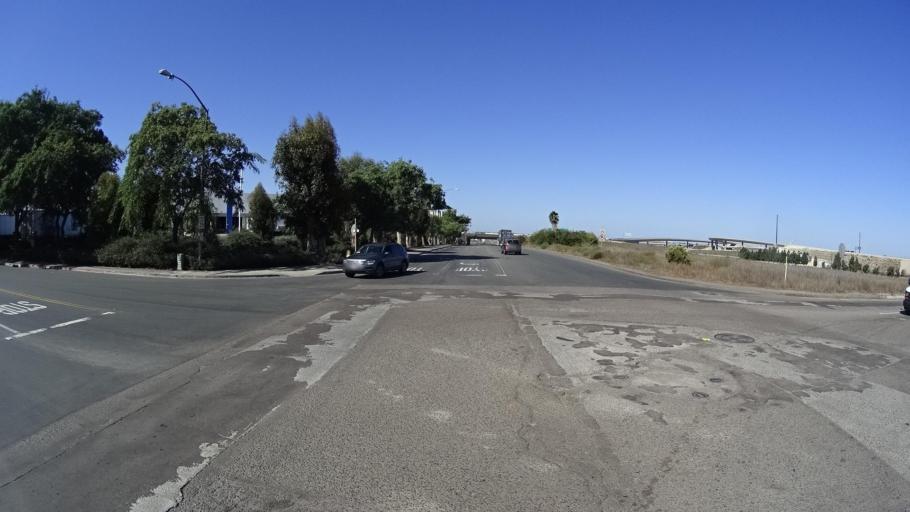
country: MX
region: Baja California
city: Tijuana
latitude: 32.5602
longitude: -116.9408
